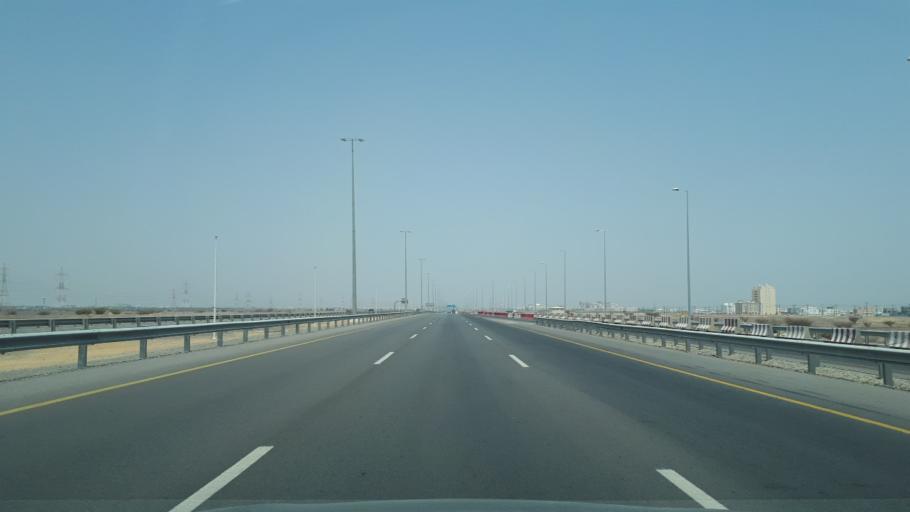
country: OM
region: Muhafazat Masqat
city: As Sib al Jadidah
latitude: 23.6301
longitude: 58.0675
